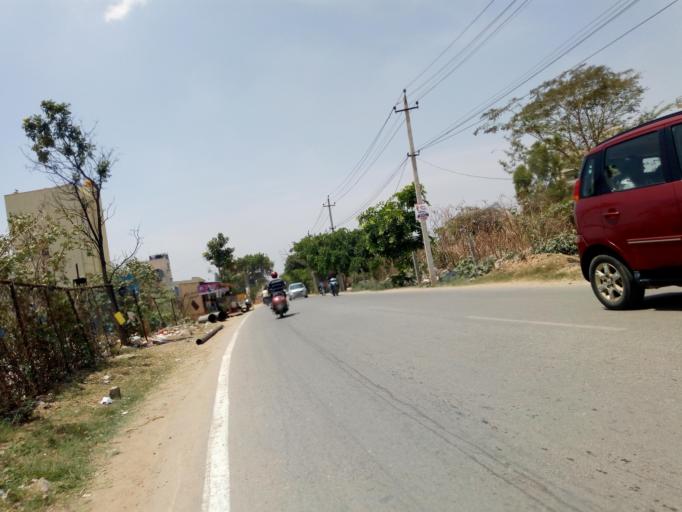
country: IN
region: Karnataka
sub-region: Bangalore Urban
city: Bangalore
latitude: 12.8836
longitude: 77.6558
